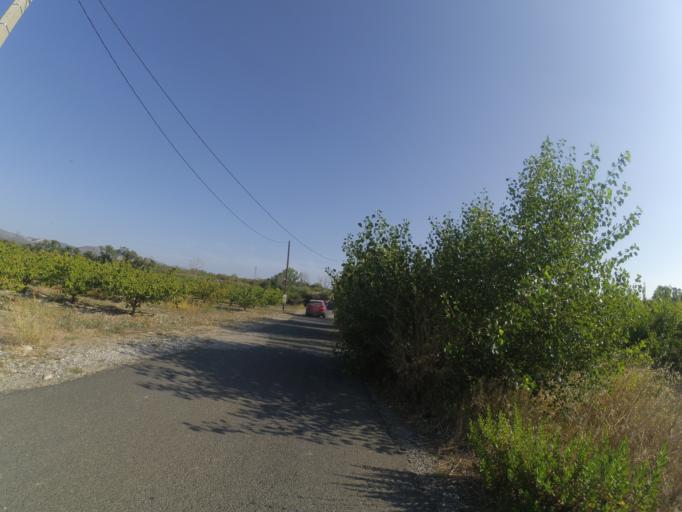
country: FR
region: Languedoc-Roussillon
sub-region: Departement des Pyrenees-Orientales
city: Peyrestortes
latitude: 42.7827
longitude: 2.8393
